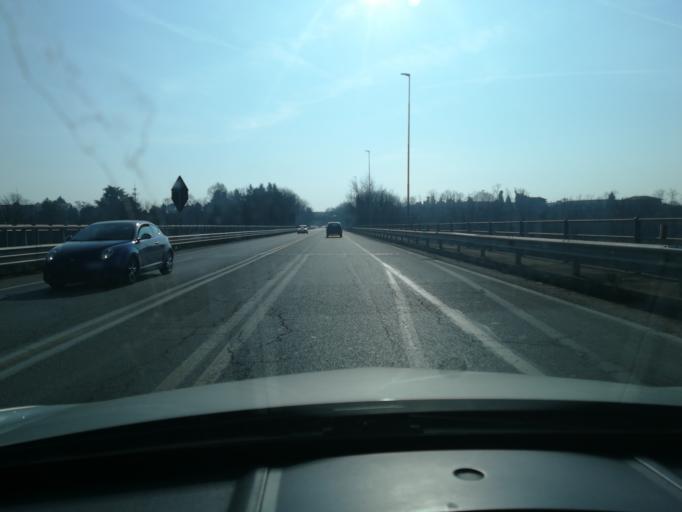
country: IT
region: Lombardy
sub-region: Provincia di Brescia
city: Palazzolo sull'Oglio
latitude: 45.5934
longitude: 9.8740
